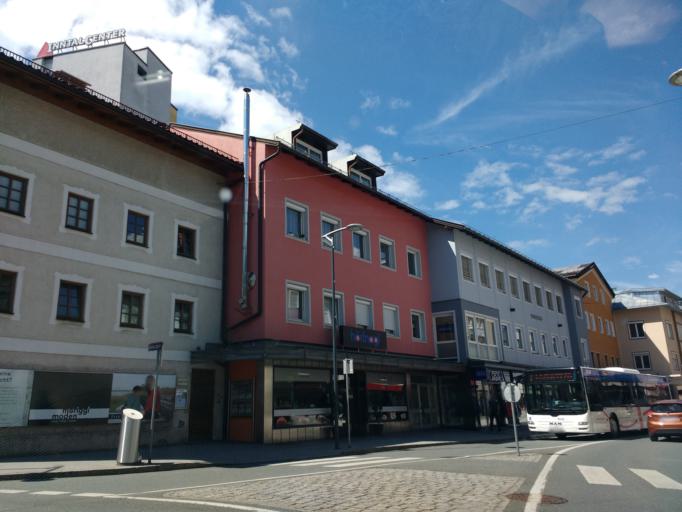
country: AT
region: Tyrol
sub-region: Politischer Bezirk Kufstein
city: Kufstein
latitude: 47.5845
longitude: 12.1715
